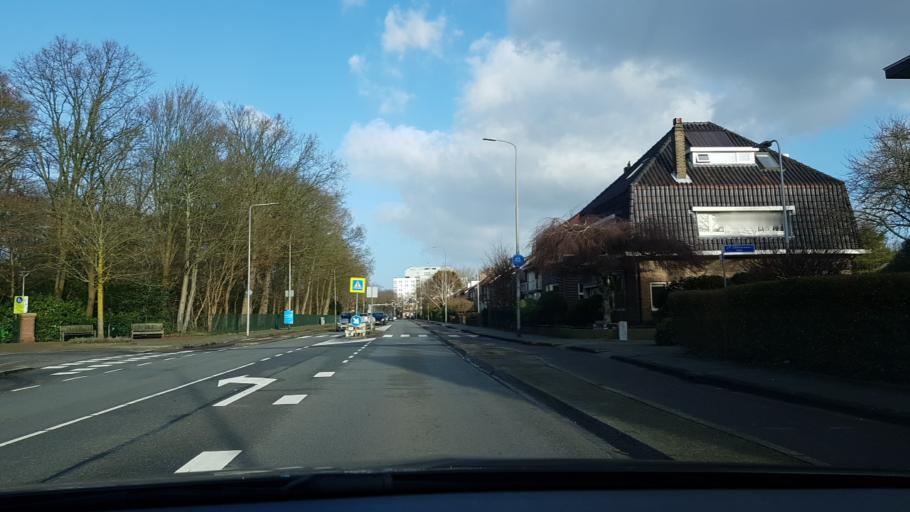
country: NL
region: South Holland
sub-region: Gemeente Teylingen
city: Sassenheim
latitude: 52.2238
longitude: 4.5247
